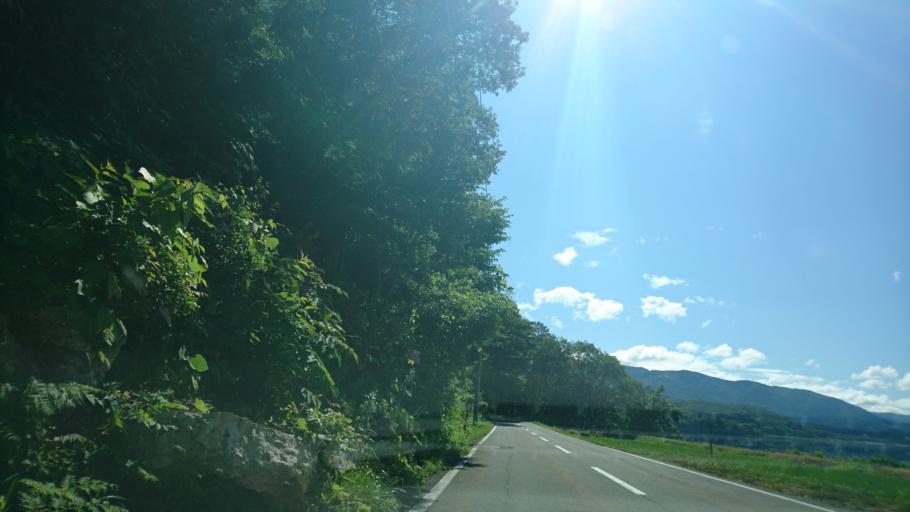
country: JP
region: Akita
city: Kakunodatemachi
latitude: 39.7484
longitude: 140.6703
